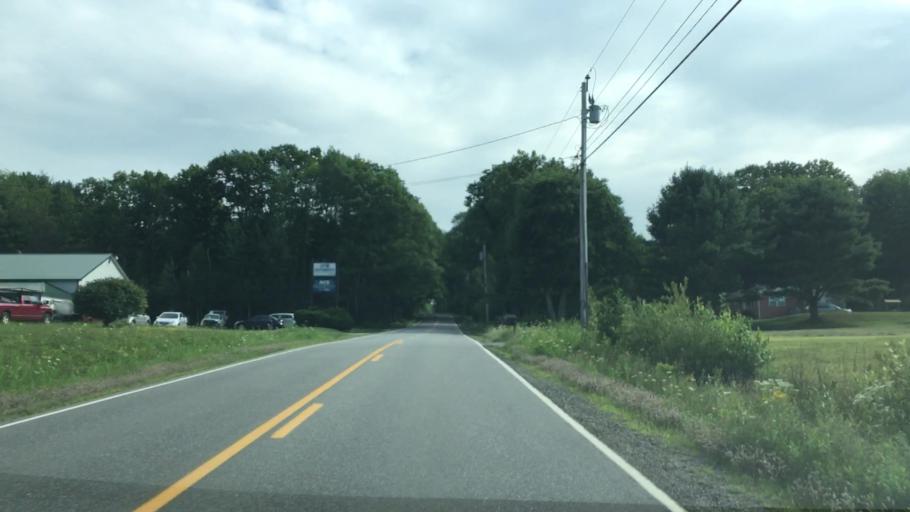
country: US
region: Maine
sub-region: Waldo County
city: Belfast
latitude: 44.3998
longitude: -69.0322
